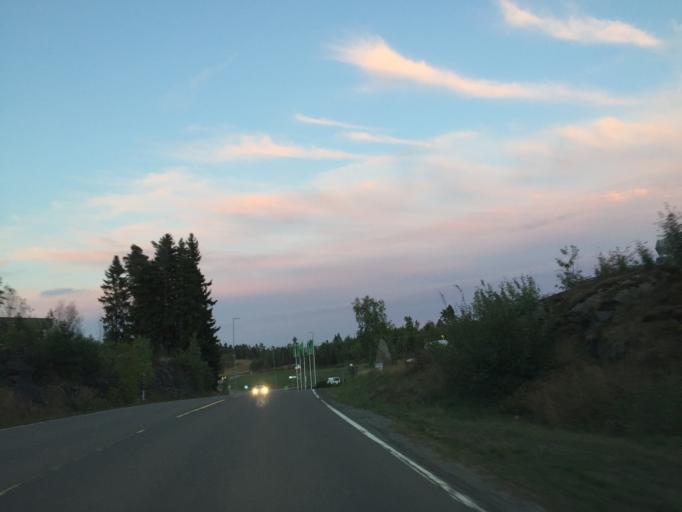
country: NO
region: Akershus
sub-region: Vestby
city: Vestby
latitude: 59.5188
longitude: 10.7099
